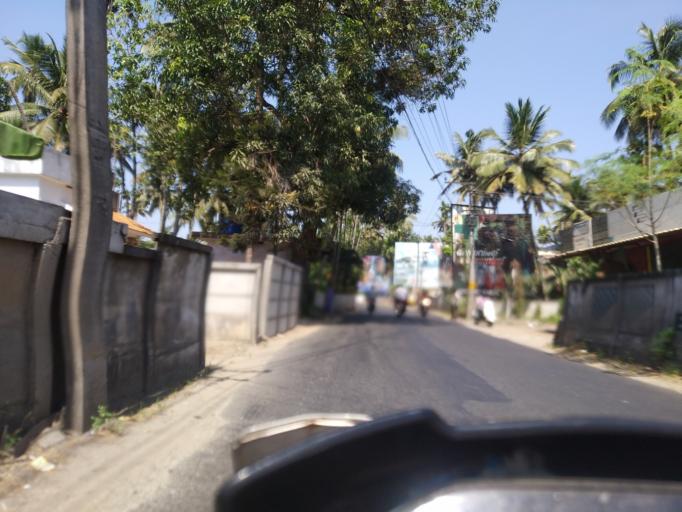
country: IN
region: Kerala
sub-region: Thrissur District
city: Kodungallur
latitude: 10.1760
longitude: 76.2117
